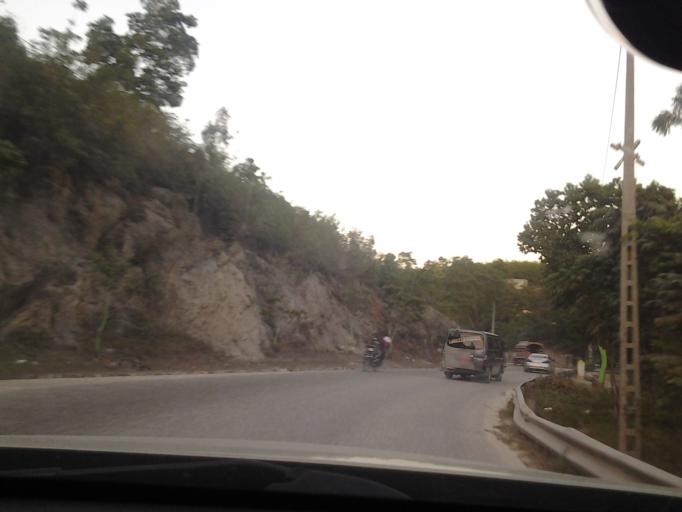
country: HT
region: Ouest
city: Leogane
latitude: 18.4397
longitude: -72.6459
